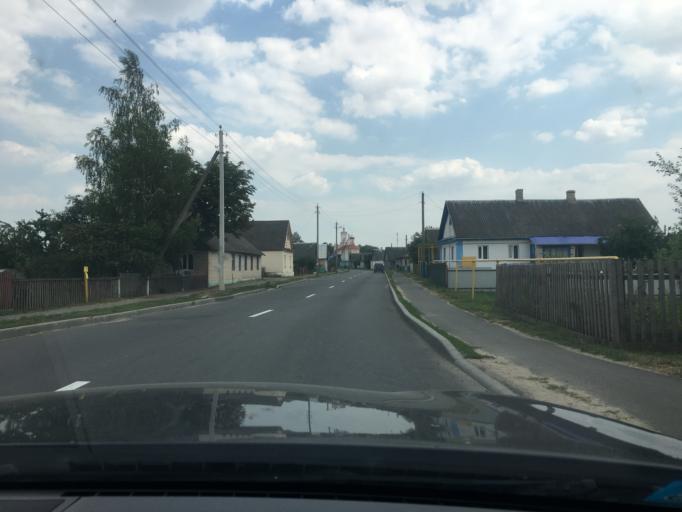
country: BY
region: Brest
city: Ruzhany
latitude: 52.8671
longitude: 24.8816
